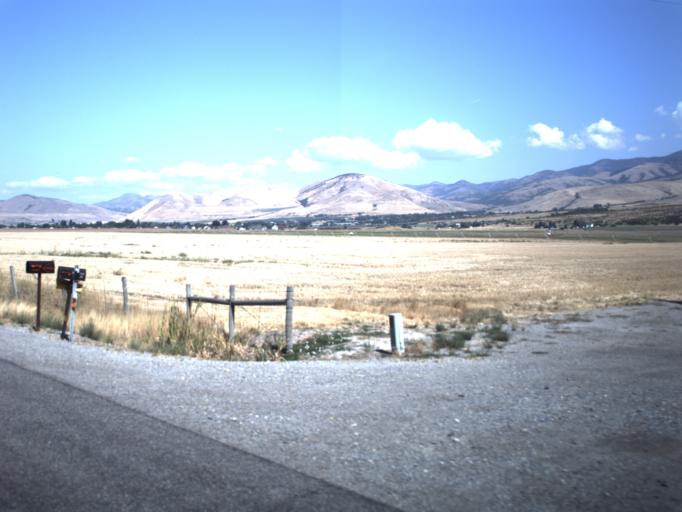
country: US
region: Utah
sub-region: Cache County
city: Lewiston
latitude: 41.9940
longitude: -111.8127
